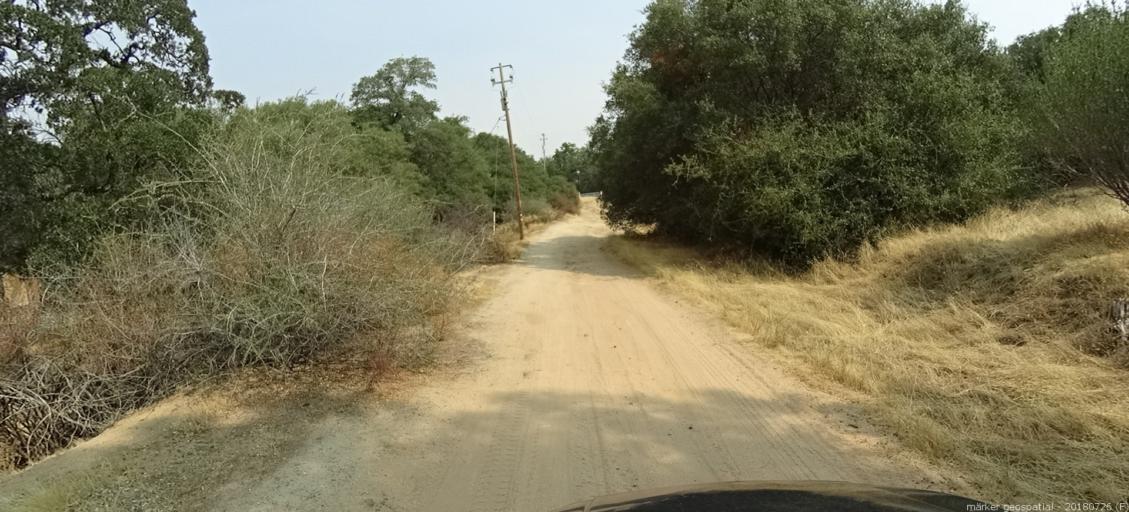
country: US
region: California
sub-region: Madera County
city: Coarsegold
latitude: 37.2377
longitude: -119.7010
